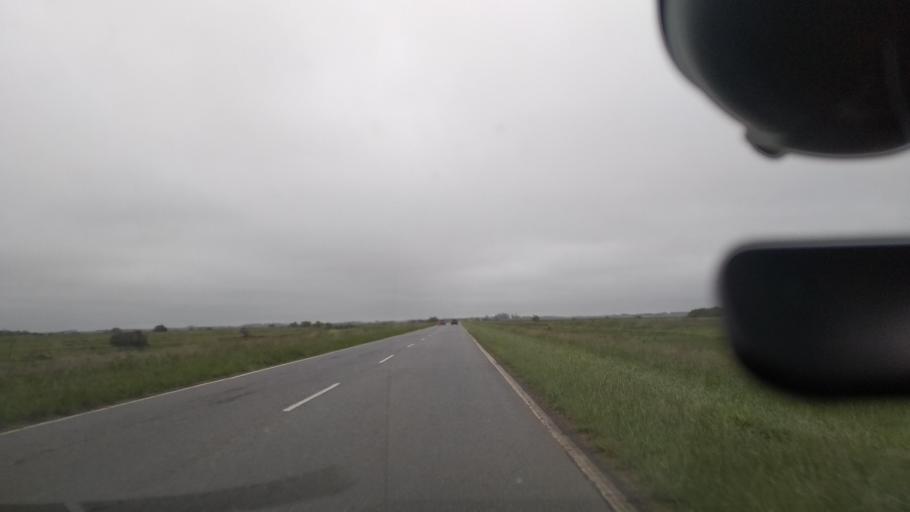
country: AR
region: Buenos Aires
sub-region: Partido de Magdalena
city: Magdalena
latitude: -35.2599
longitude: -57.6386
